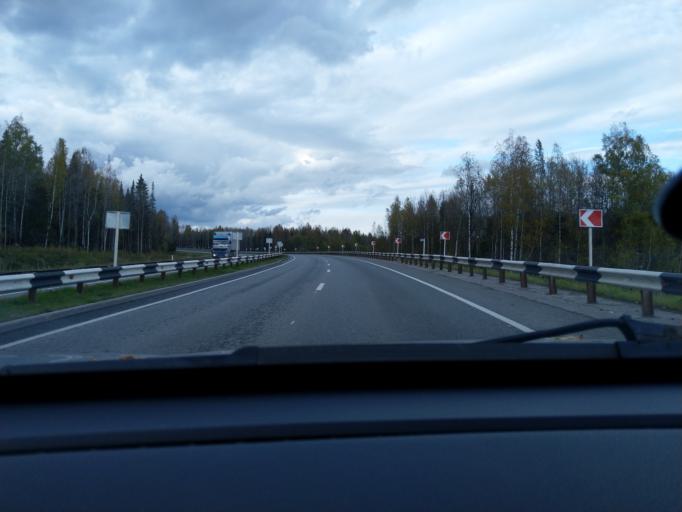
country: RU
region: Perm
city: Polazna
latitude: 58.3329
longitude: 56.4792
